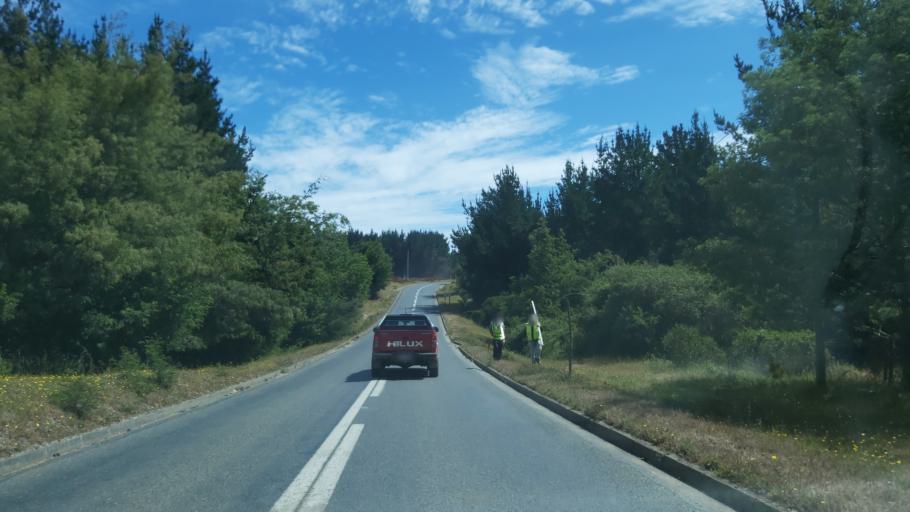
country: CL
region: Maule
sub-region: Provincia de Talca
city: Constitucion
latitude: -35.5484
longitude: -72.5657
